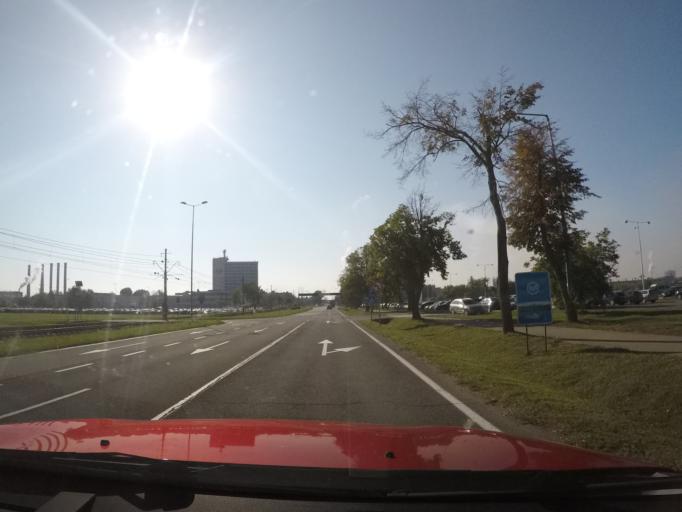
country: SK
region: Kosicky
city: Kosice
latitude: 48.6256
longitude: 21.1874
